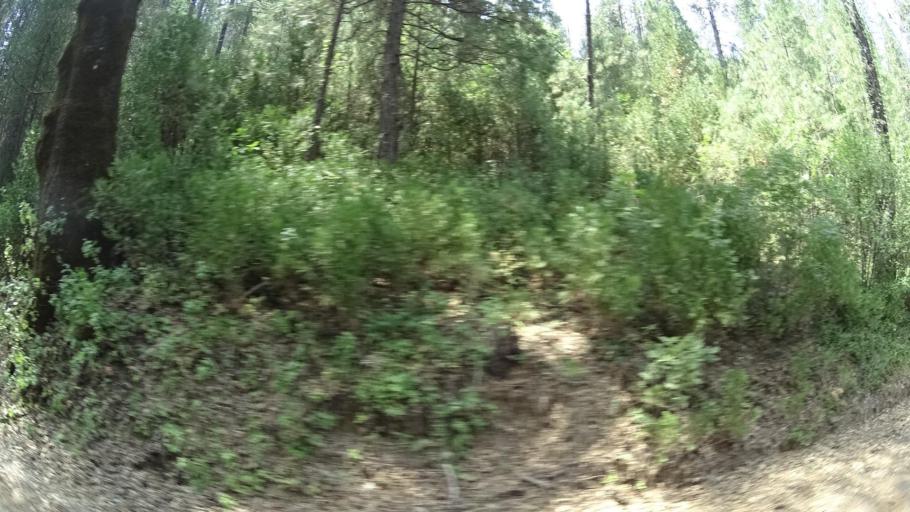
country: US
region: California
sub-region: Mariposa County
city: Midpines
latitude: 37.7523
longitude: -120.0516
